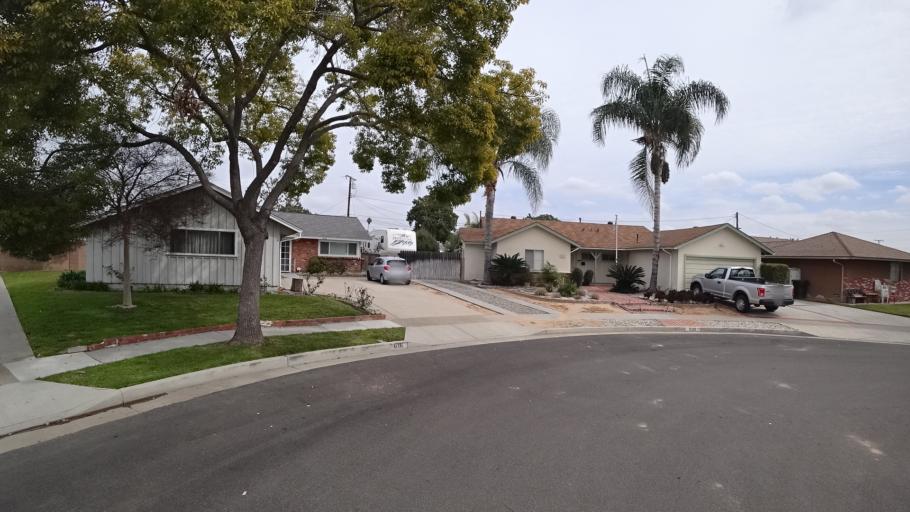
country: US
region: California
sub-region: Orange County
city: Stanton
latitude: 33.8240
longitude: -117.9876
